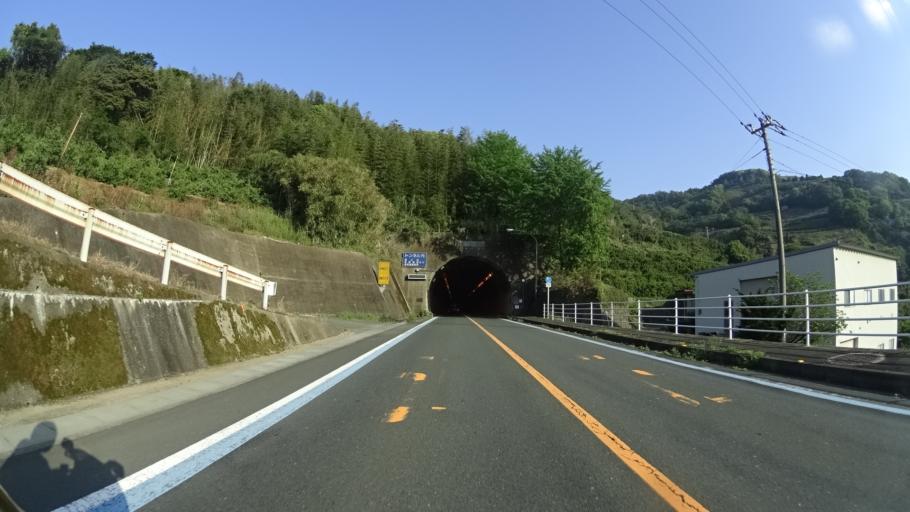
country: JP
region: Ehime
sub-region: Nishiuwa-gun
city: Ikata-cho
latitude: 33.4900
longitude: 132.3861
